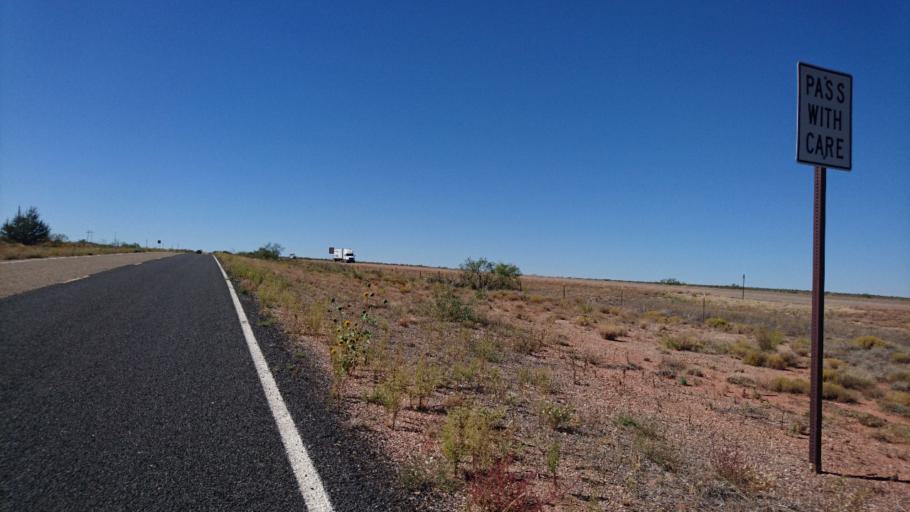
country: US
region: New Mexico
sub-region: Quay County
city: Tucumcari
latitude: 35.0820
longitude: -104.1147
